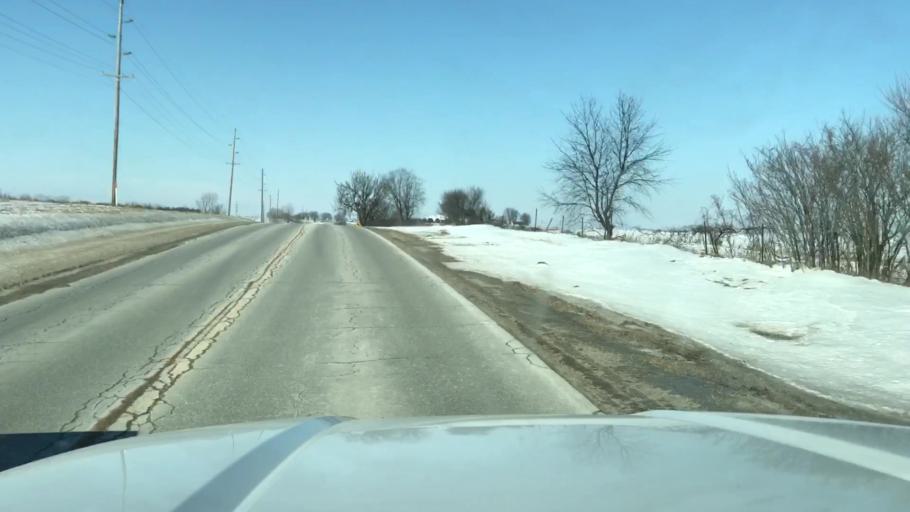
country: US
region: Missouri
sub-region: Andrew County
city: Savannah
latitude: 39.9594
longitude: -94.8531
